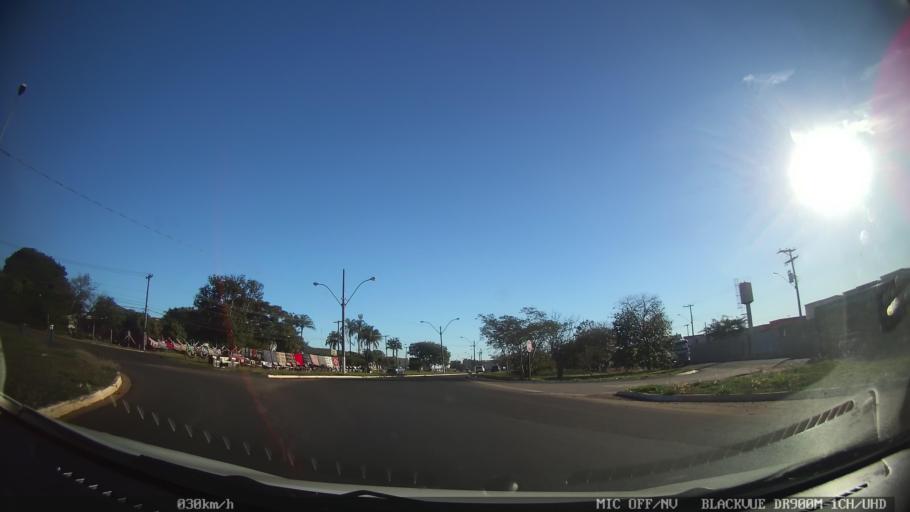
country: BR
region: Sao Paulo
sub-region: Americo Brasiliense
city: Americo Brasiliense
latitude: -21.7438
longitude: -48.1254
